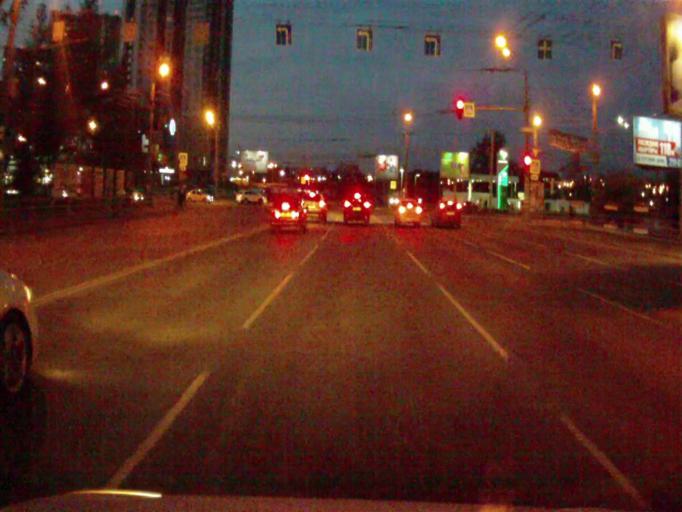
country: RU
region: Chelyabinsk
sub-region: Gorod Chelyabinsk
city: Chelyabinsk
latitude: 55.1671
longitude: 61.3807
